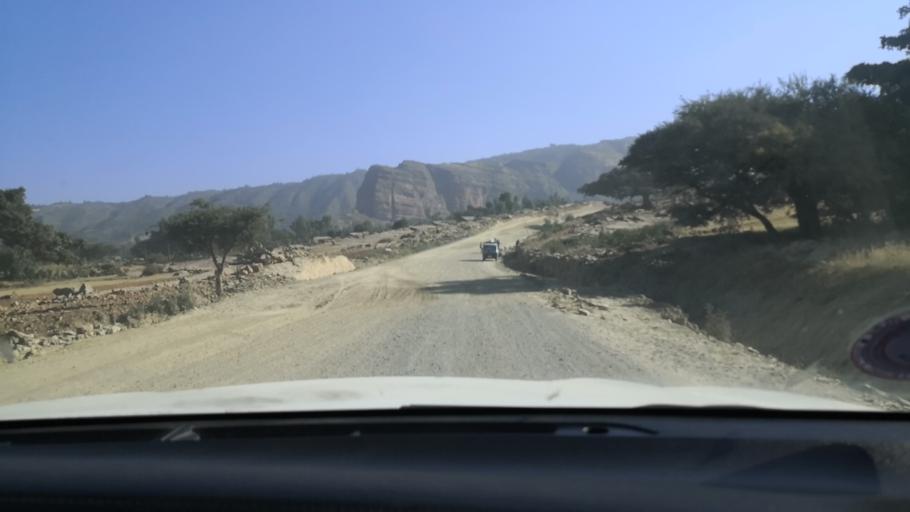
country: ET
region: Tigray
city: Mekele
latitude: 13.8431
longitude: 39.5297
